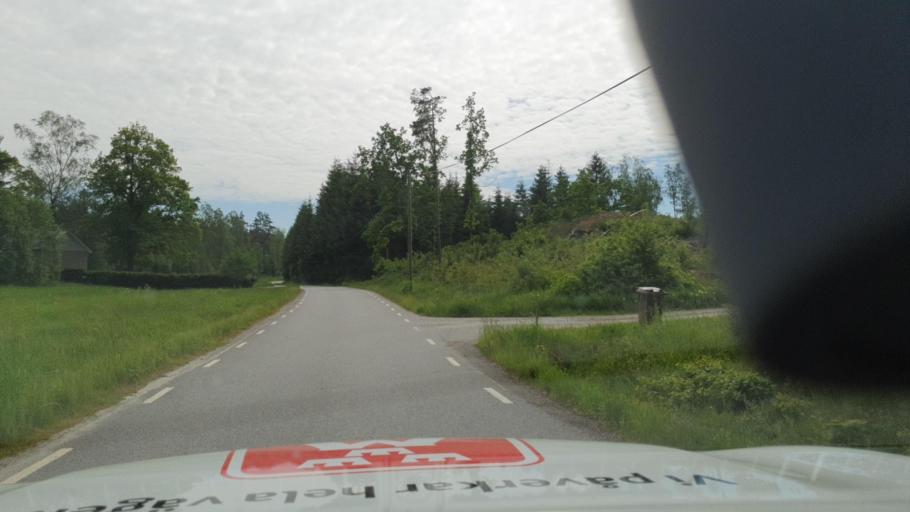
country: SE
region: Vaestra Goetaland
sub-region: Vanersborgs Kommun
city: Vargon
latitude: 58.2647
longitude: 12.5016
